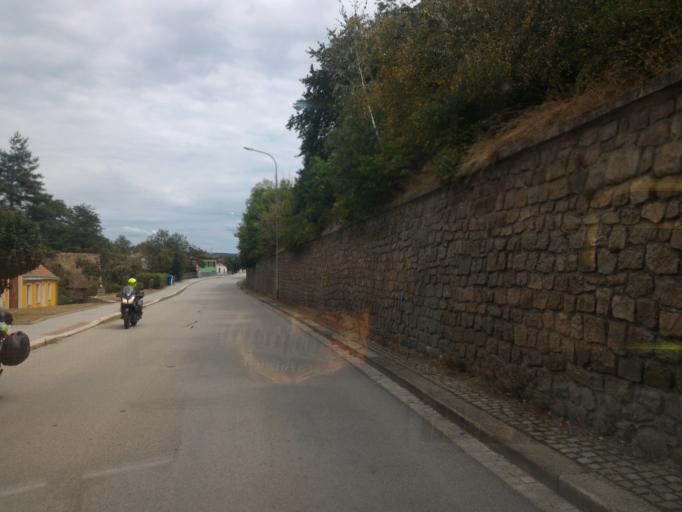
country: CZ
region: Jihocesky
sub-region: Okres Jindrichuv Hradec
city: Dacice
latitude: 49.0784
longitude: 15.4430
